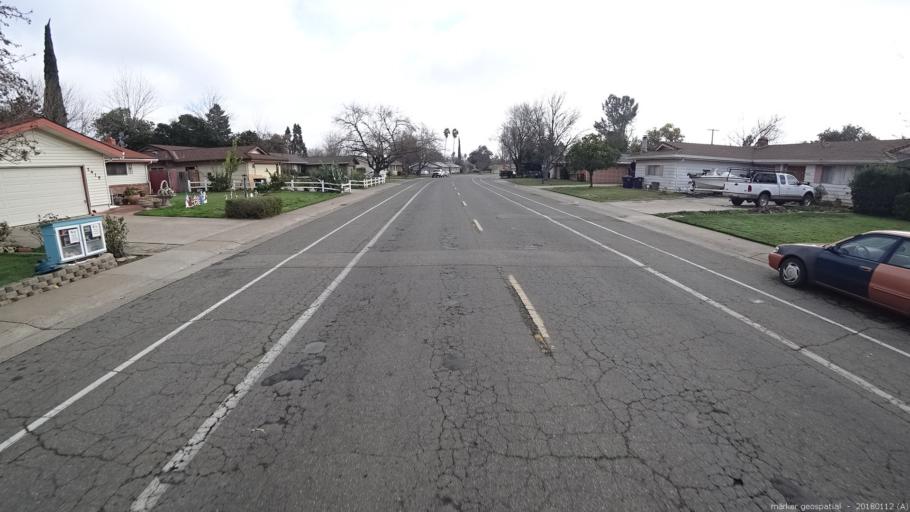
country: US
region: California
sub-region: Sacramento County
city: Rancho Cordova
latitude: 38.6051
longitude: -121.2938
